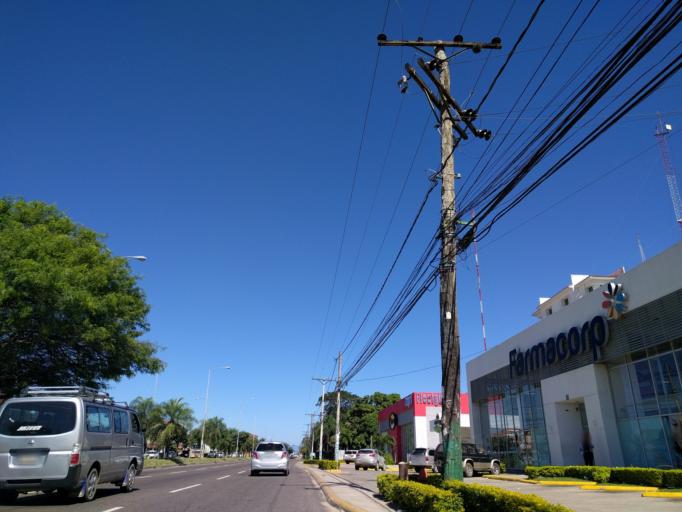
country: BO
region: Santa Cruz
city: Santa Cruz de la Sierra
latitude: -17.8201
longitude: -63.2177
